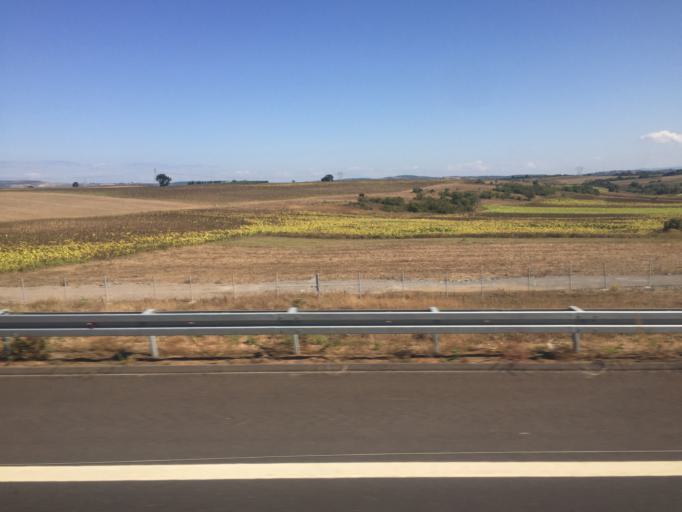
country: TR
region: Bursa
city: Mahmudiye
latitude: 40.2708
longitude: 28.6178
